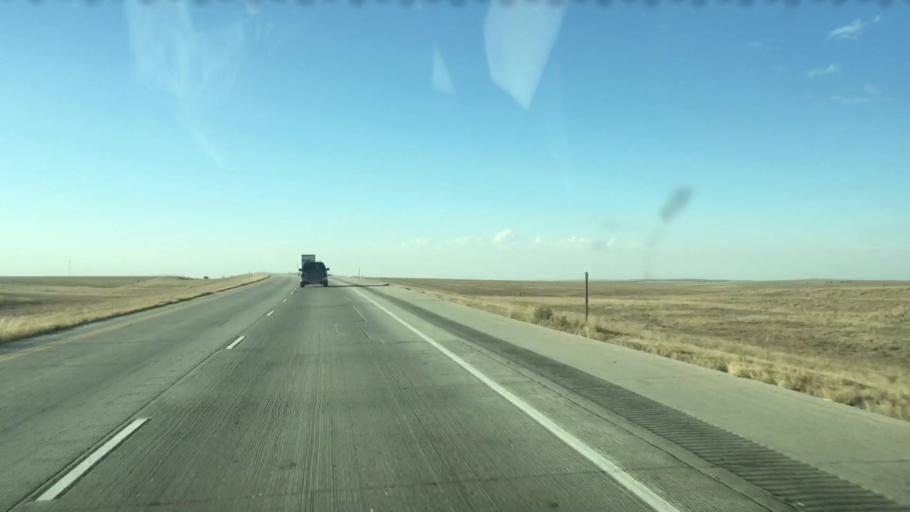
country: US
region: Colorado
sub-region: Lincoln County
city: Limon
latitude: 39.4145
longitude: -103.9028
